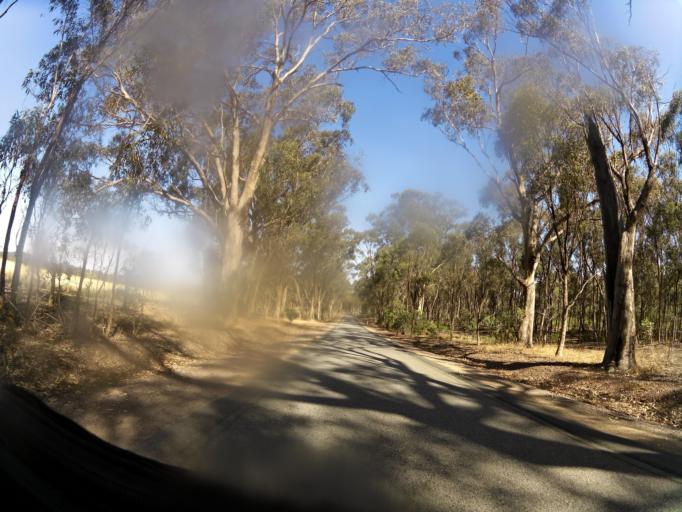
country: AU
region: Victoria
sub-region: Campaspe
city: Kyabram
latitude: -36.8825
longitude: 145.0949
